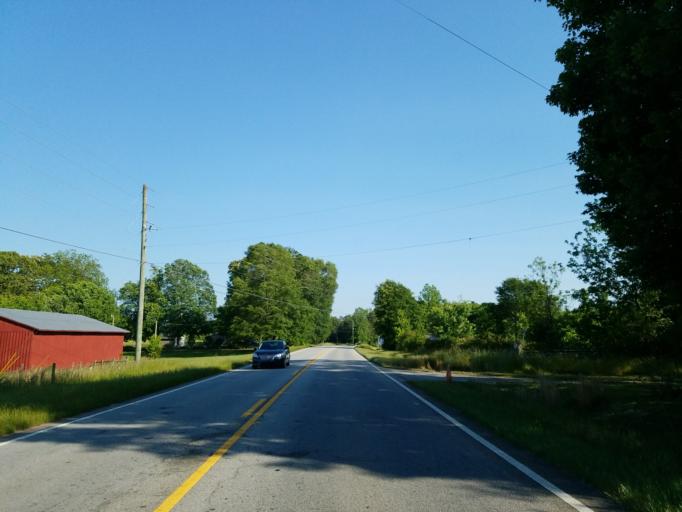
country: US
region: Georgia
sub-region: Carroll County
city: Temple
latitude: 33.8270
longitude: -84.9783
